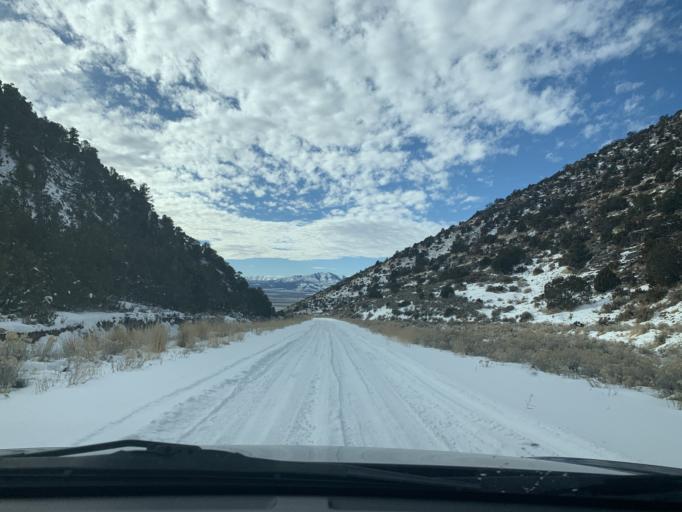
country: US
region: Utah
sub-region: Tooele County
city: Tooele
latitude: 40.3144
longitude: -112.2353
